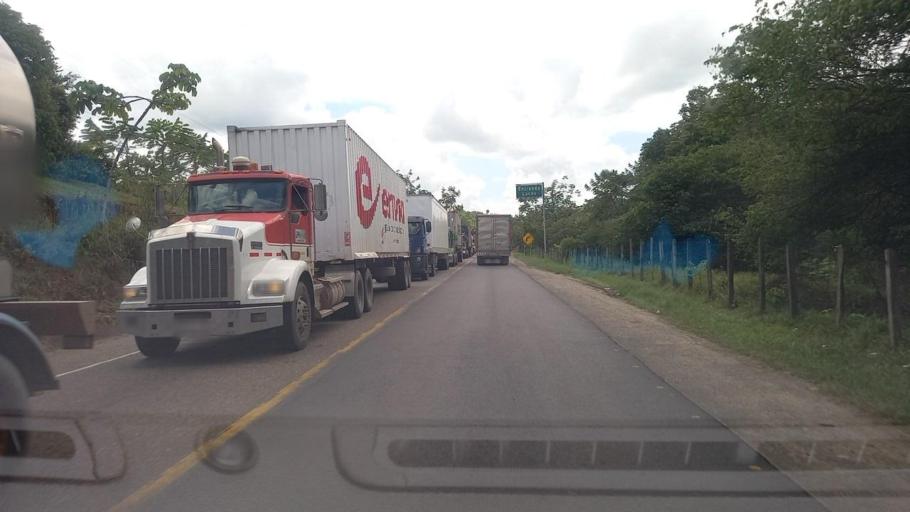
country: CO
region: Santander
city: Puerto Parra
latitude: 6.6437
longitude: -73.9539
